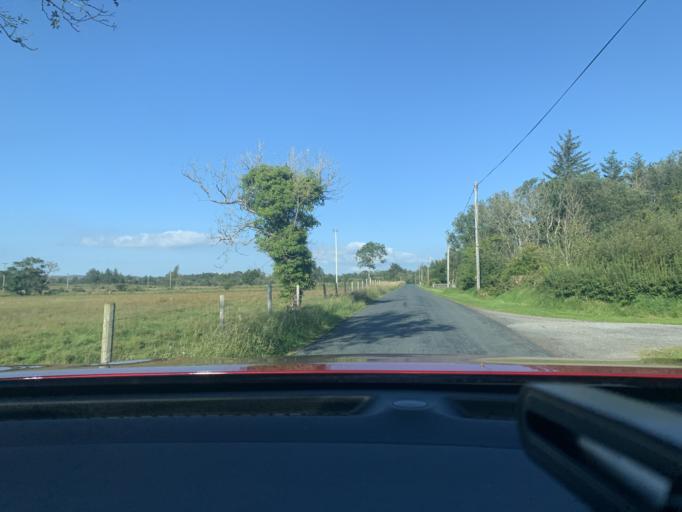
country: IE
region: Connaught
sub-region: Sligo
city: Tobercurry
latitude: 54.1316
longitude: -8.7202
